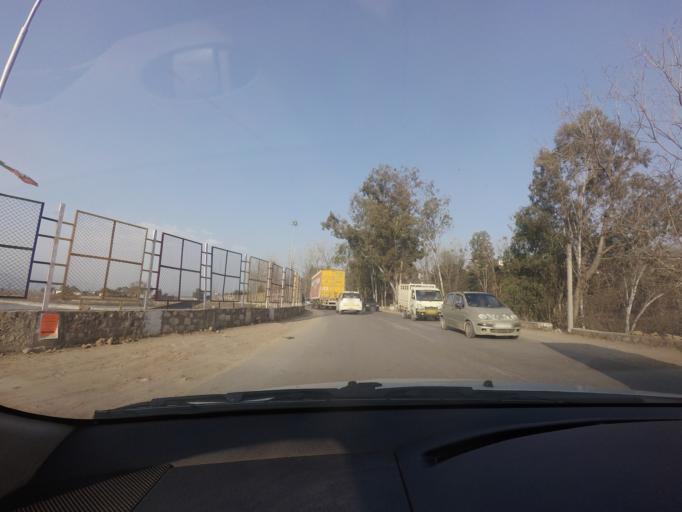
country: IN
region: Himachal Pradesh
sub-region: Mandi
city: Sundarnagar
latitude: 31.5379
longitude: 76.8947
